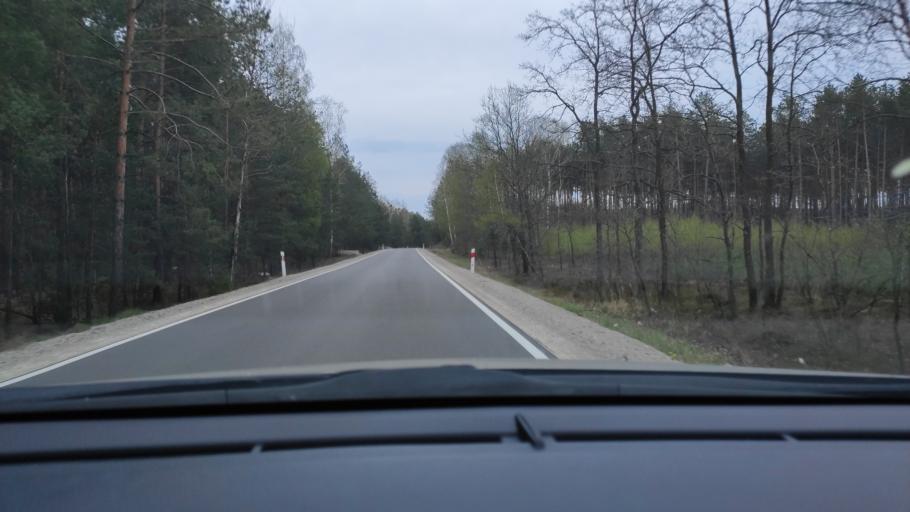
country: PL
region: Masovian Voivodeship
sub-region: Powiat zwolenski
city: Zwolen
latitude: 51.4074
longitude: 21.5240
